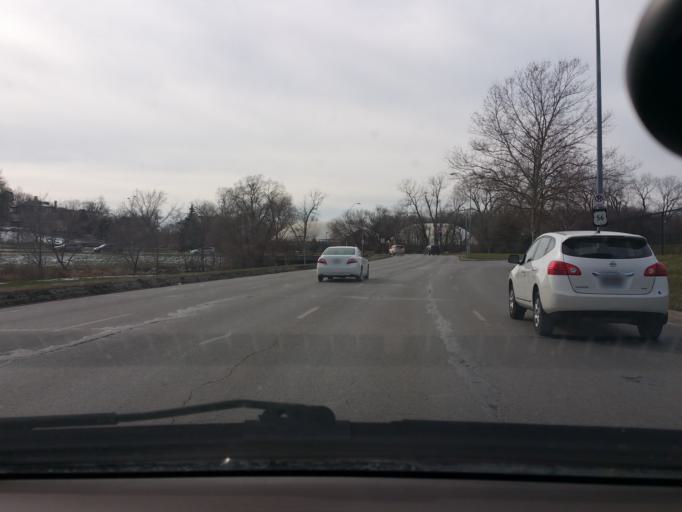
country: US
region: Kansas
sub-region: Johnson County
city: Westwood
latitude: 39.0339
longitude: -94.6040
